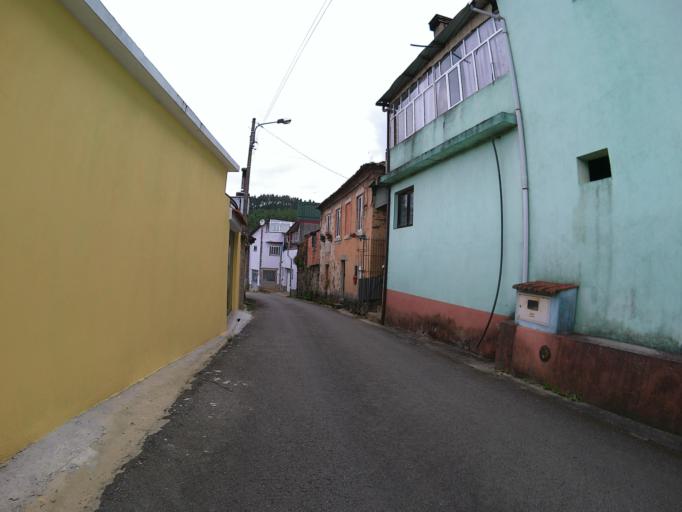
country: PT
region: Aveiro
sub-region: Albergaria-A-Velha
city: Branca
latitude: 40.7399
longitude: -8.4434
